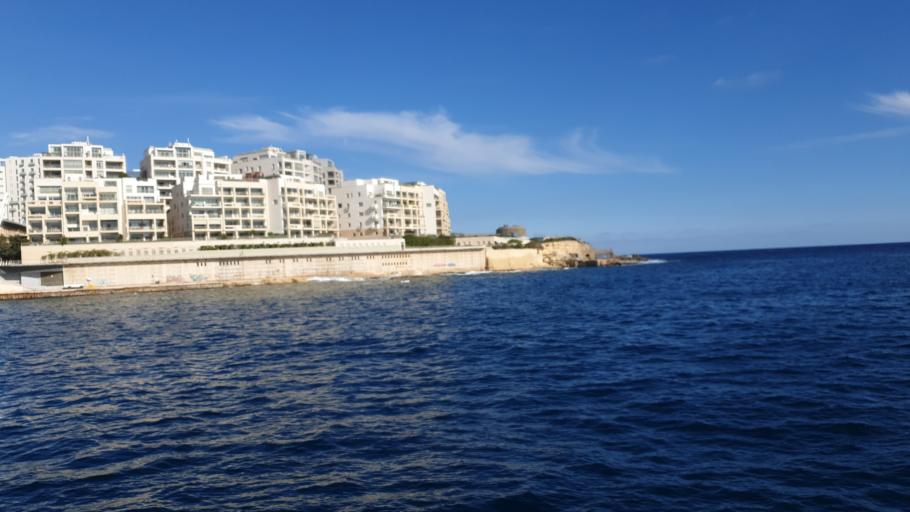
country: MT
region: Il-Belt Valletta
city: Valletta
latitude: 35.9047
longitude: 14.5091
